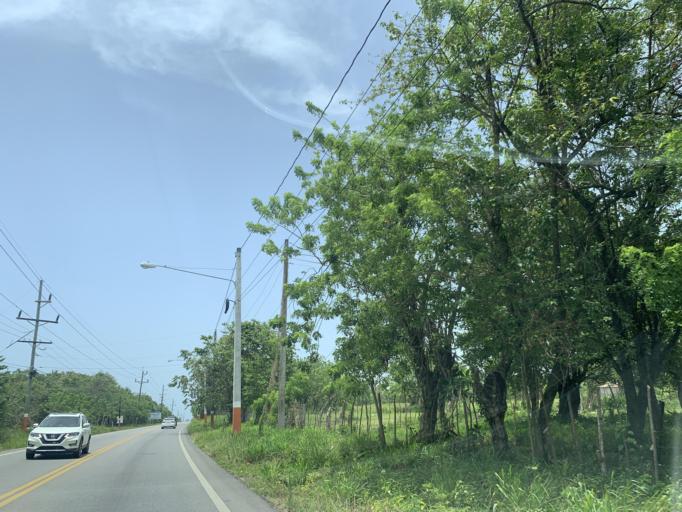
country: DO
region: Puerto Plata
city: Cabarete
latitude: 19.7785
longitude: -70.4764
